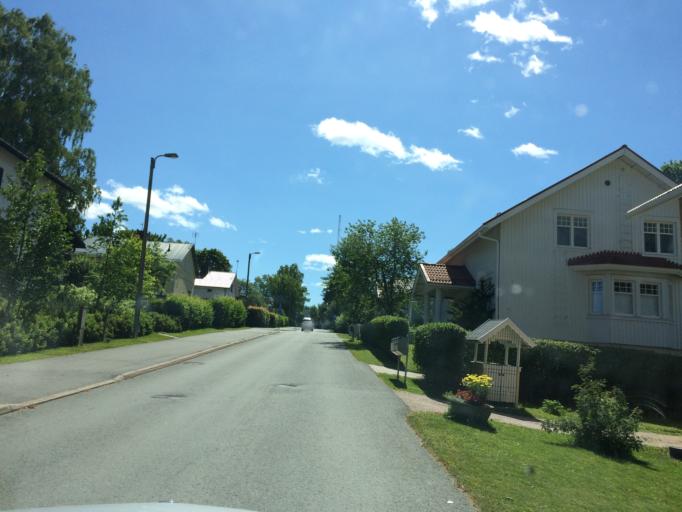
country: FI
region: Haeme
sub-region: Haemeenlinna
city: Haemeenlinna
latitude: 60.9903
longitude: 24.4460
